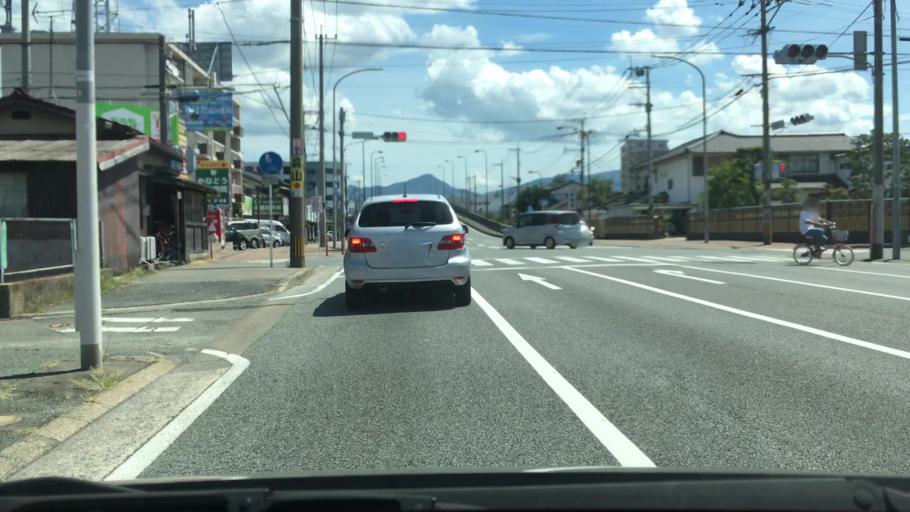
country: JP
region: Fukuoka
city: Fukuoka-shi
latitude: 33.5619
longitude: 130.4374
